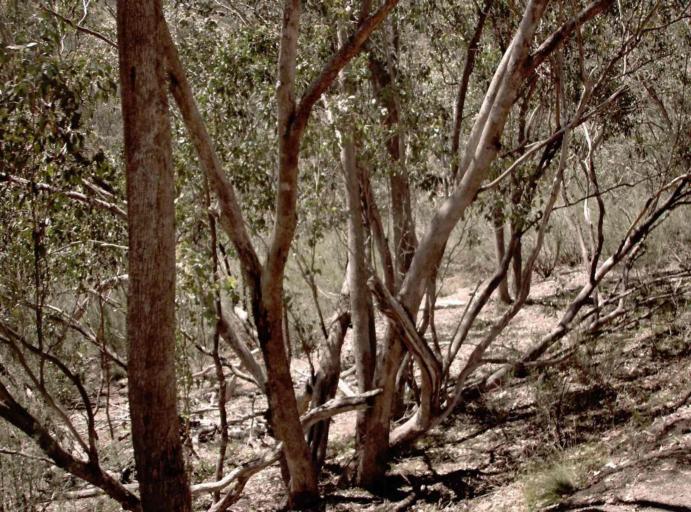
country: AU
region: New South Wales
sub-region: Snowy River
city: Jindabyne
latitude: -37.0803
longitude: 148.4512
